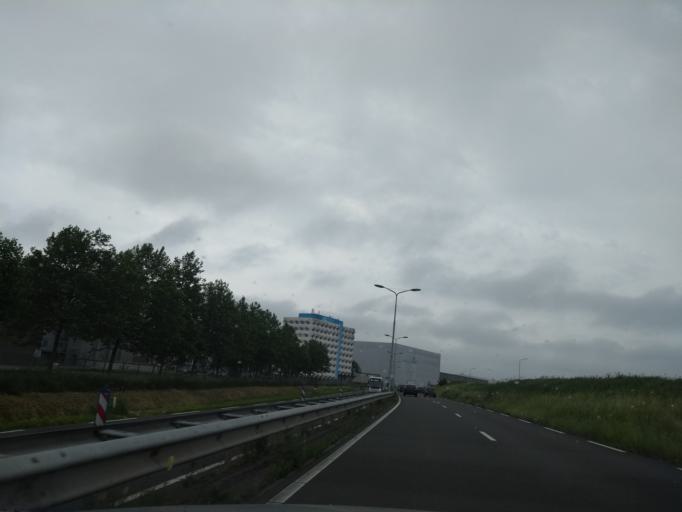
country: NL
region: North Holland
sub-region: Gemeente Aalsmeer
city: Aalsmeer
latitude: 52.2973
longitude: 4.7937
